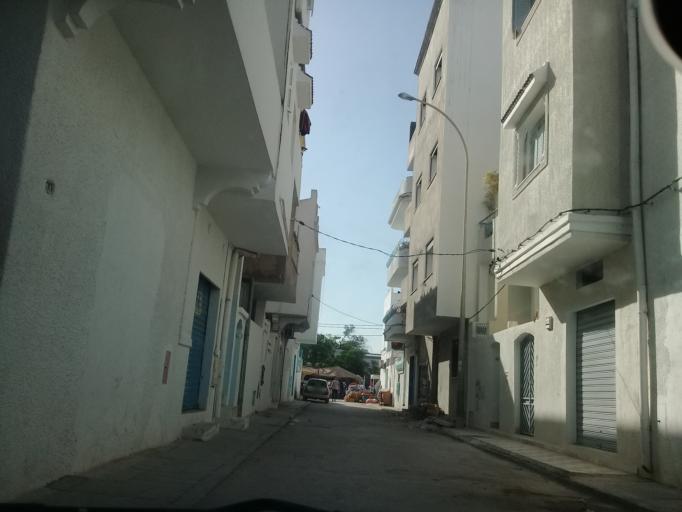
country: TN
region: Ariana
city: Ariana
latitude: 36.8320
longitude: 10.1941
